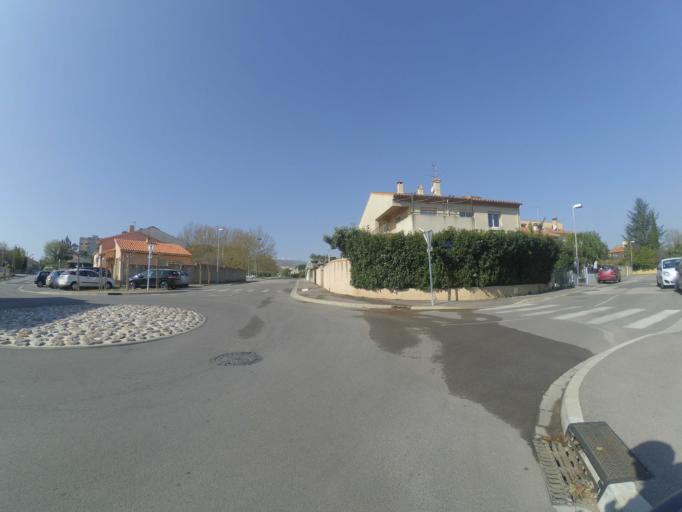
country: FR
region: Languedoc-Roussillon
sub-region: Departement des Pyrenees-Orientales
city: Thuir
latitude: 42.6306
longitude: 2.7530
